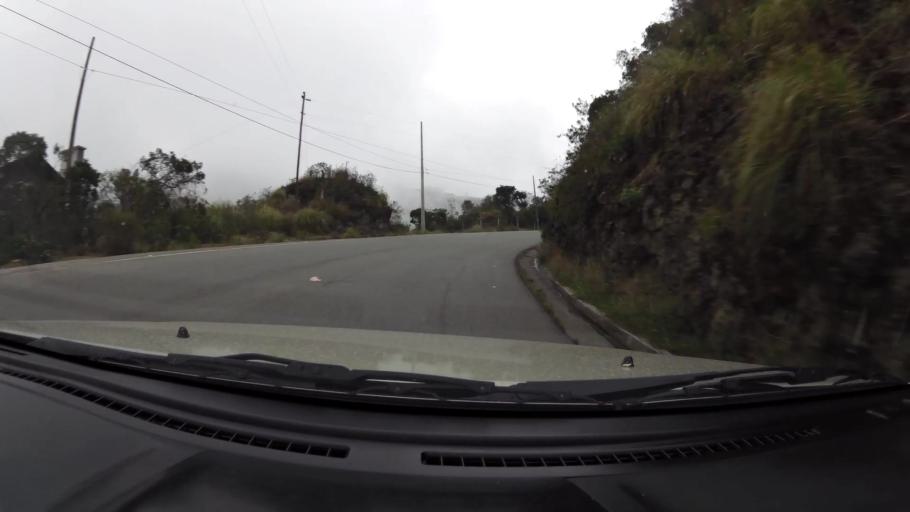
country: EC
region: Canar
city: Canar
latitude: -2.4513
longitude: -79.0052
